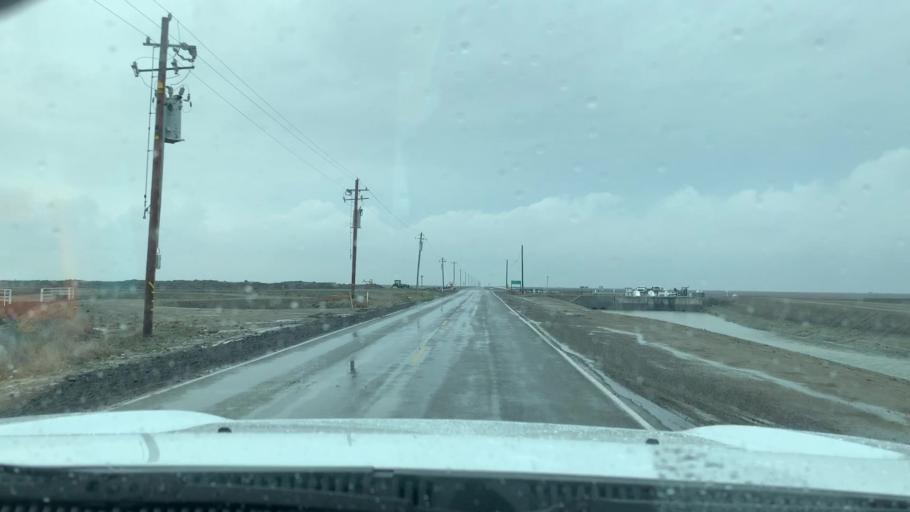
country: US
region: California
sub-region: Tulare County
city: Alpaugh
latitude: 35.9361
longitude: -119.5731
